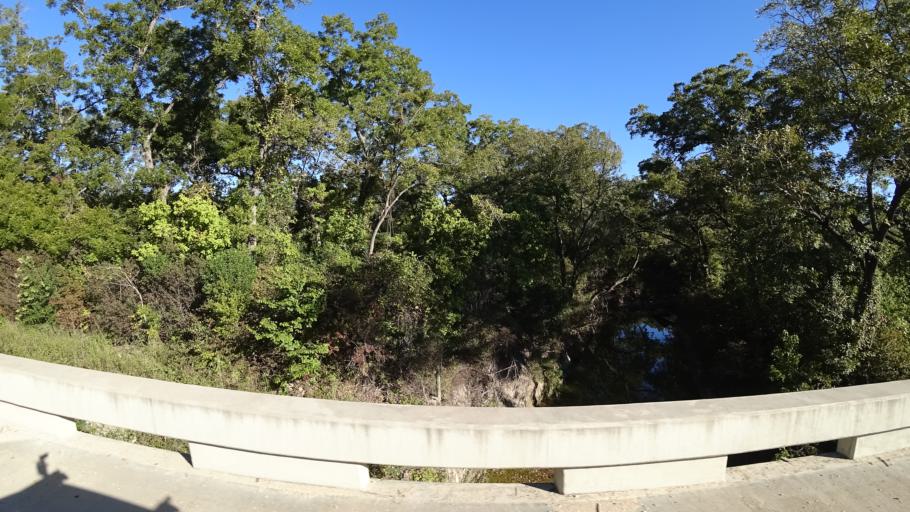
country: US
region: Texas
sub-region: Travis County
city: Manor
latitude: 30.3226
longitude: -97.6505
